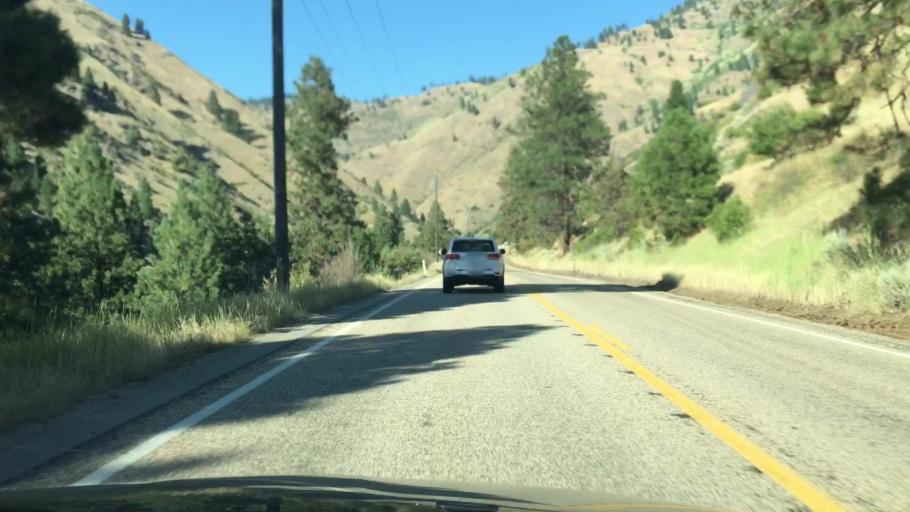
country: US
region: Idaho
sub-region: Boise County
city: Idaho City
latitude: 44.0221
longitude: -116.1492
